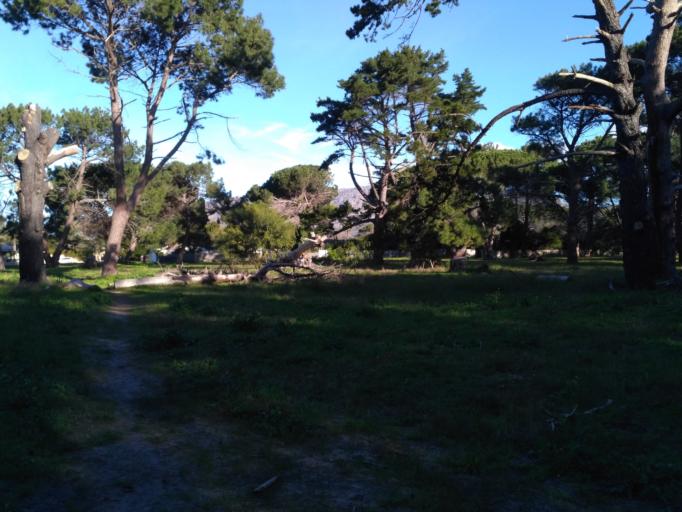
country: ZA
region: Western Cape
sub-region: City of Cape Town
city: Bergvliet
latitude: -34.0562
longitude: 18.4385
